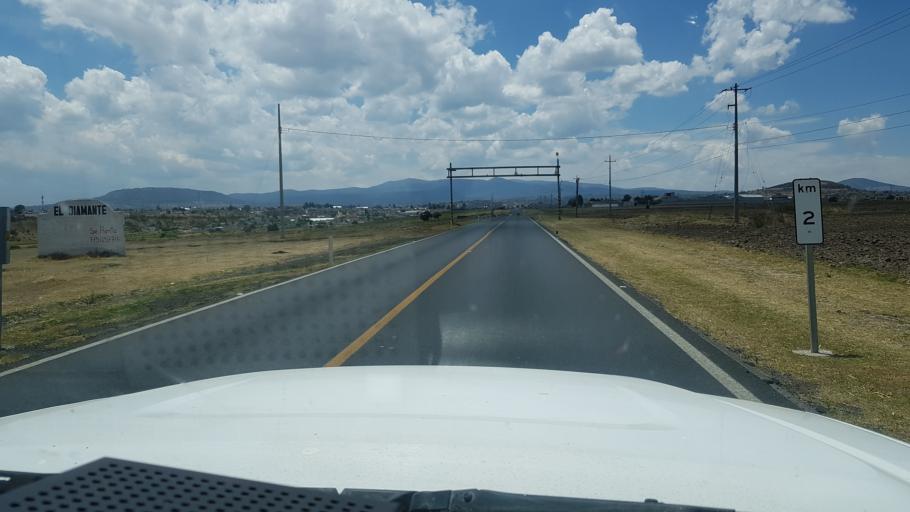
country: MX
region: Hidalgo
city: Calpulalpan
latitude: 19.6064
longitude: -98.5626
